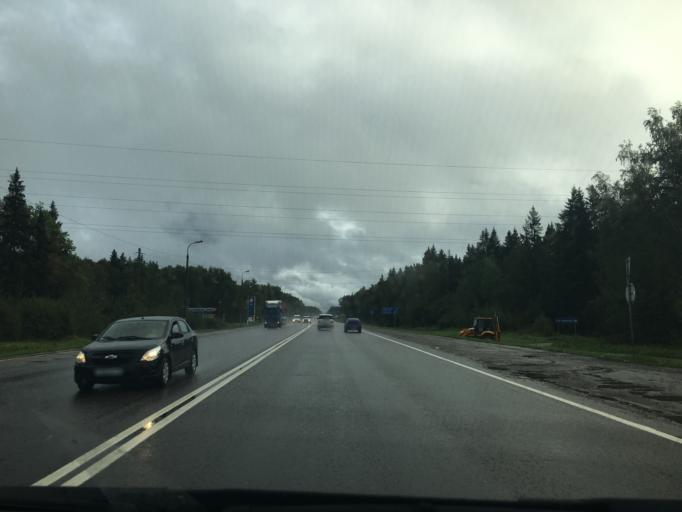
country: RU
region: Kaluga
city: Balabanovo
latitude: 55.1620
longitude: 36.6675
